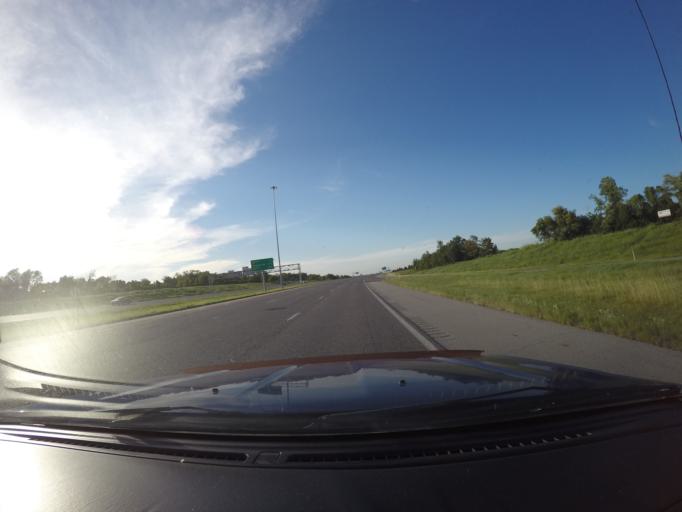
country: US
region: Kansas
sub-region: Wyandotte County
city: Edwardsville
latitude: 39.1316
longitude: -94.8176
